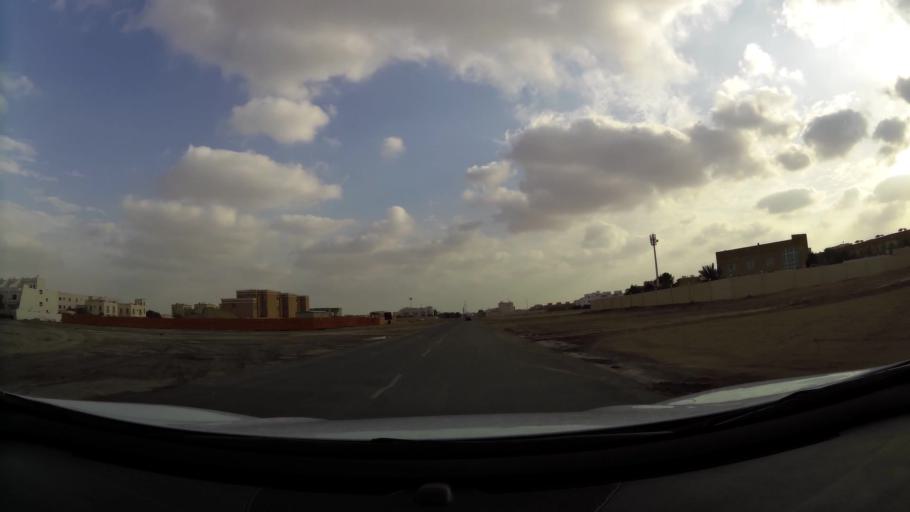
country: AE
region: Abu Dhabi
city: Abu Dhabi
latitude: 24.3665
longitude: 54.5450
